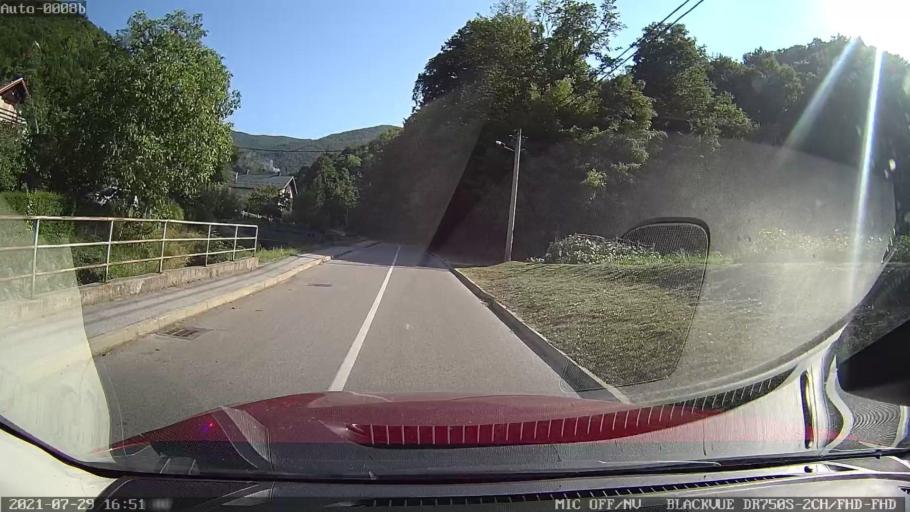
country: HR
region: Varazdinska
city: Ivanec
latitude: 46.2090
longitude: 16.1319
